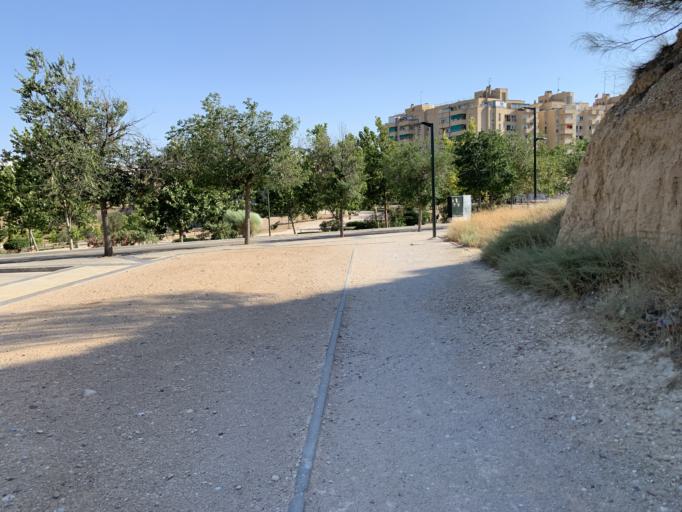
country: ES
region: Aragon
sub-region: Provincia de Zaragoza
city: Zaragoza
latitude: 41.6249
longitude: -0.8729
